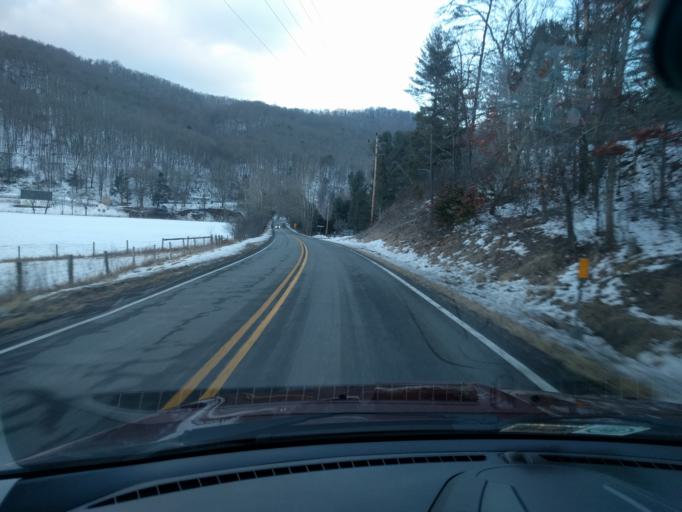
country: US
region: Virginia
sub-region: Bath County
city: Warm Springs
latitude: 38.0754
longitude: -79.8427
